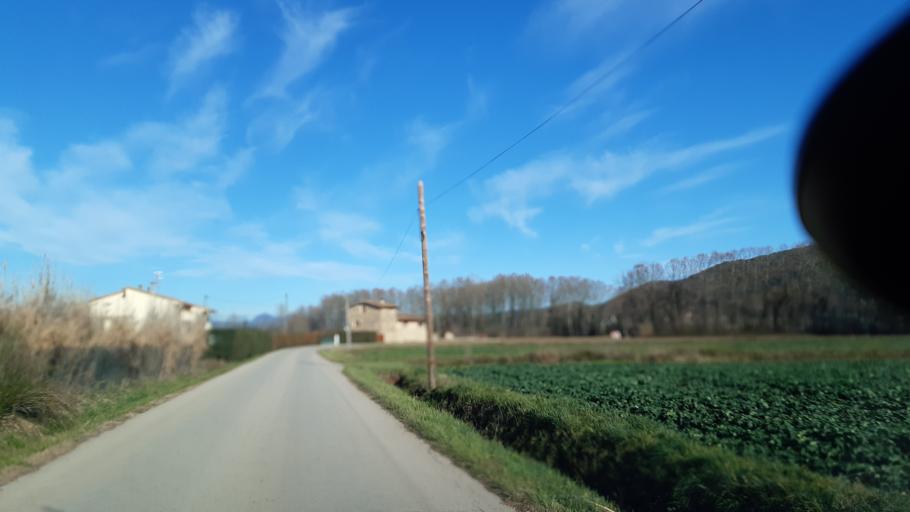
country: ES
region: Catalonia
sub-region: Provincia de Girona
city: Bas
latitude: 42.1421
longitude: 2.4465
